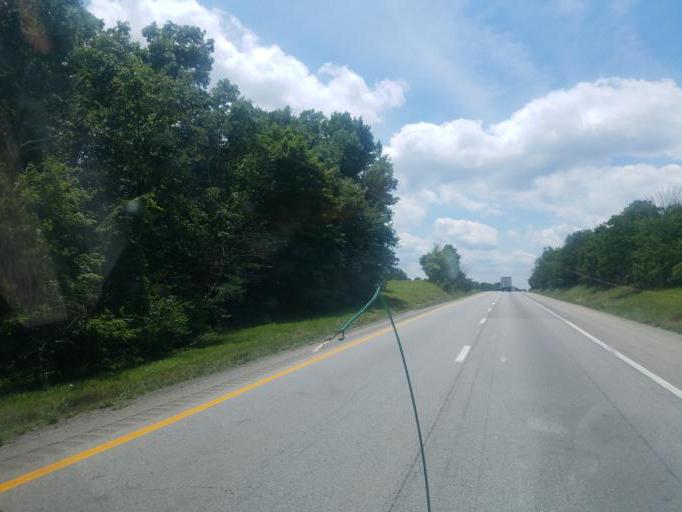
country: US
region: Kentucky
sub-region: Oldham County
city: La Grange
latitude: 38.4148
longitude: -85.3437
